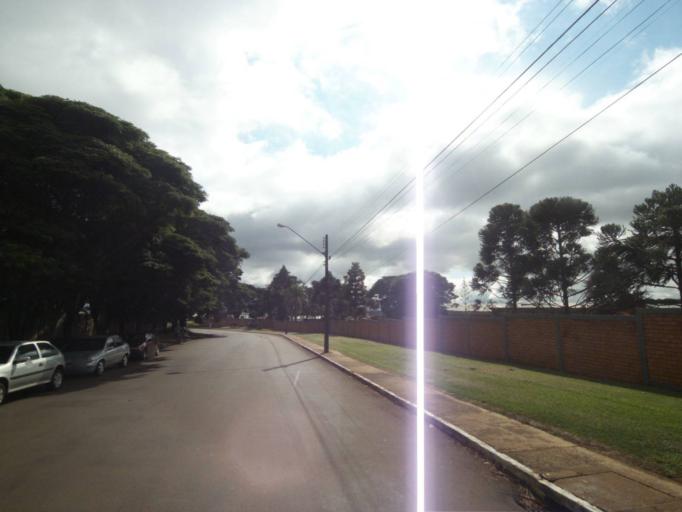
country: BR
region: Parana
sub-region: Campo Mourao
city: Campo Mourao
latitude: -24.0354
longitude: -52.3647
